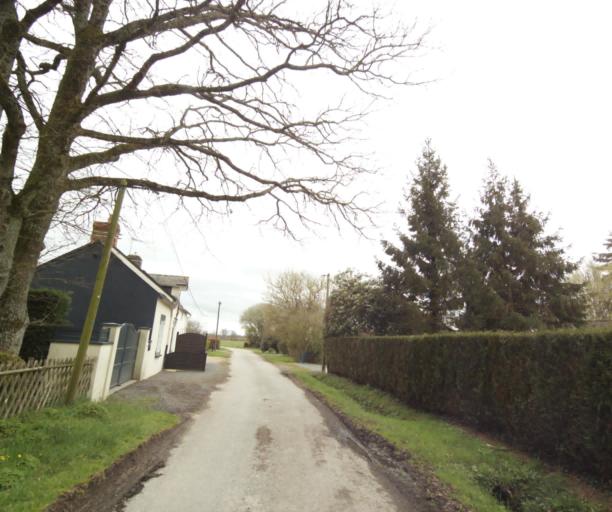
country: FR
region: Pays de la Loire
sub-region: Departement de la Loire-Atlantique
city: Bouvron
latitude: 47.4337
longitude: -1.8502
